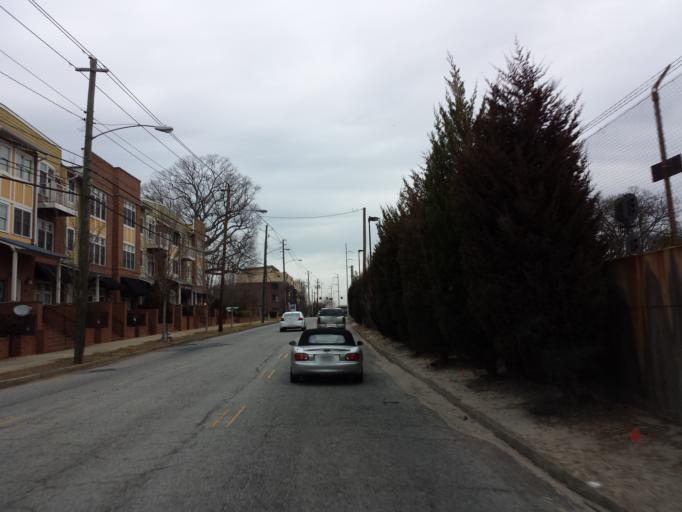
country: US
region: Georgia
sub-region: DeKalb County
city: Druid Hills
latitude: 33.7609
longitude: -84.3466
